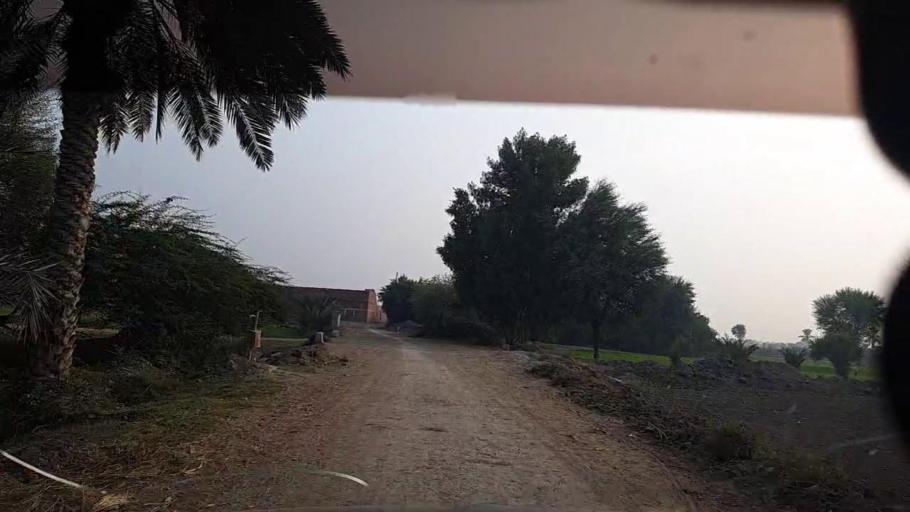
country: PK
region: Sindh
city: Gambat
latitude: 27.4331
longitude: 68.5976
